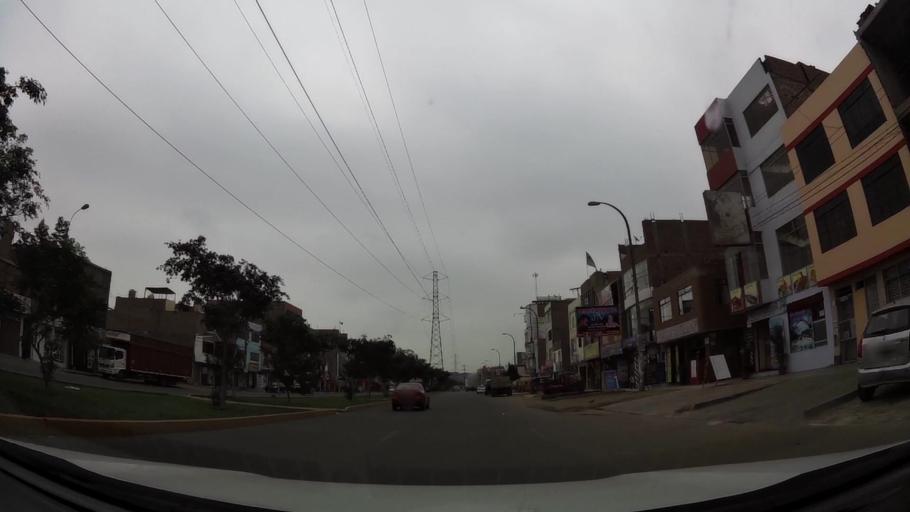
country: PE
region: Lima
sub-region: Lima
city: Independencia
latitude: -11.9713
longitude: -77.0772
